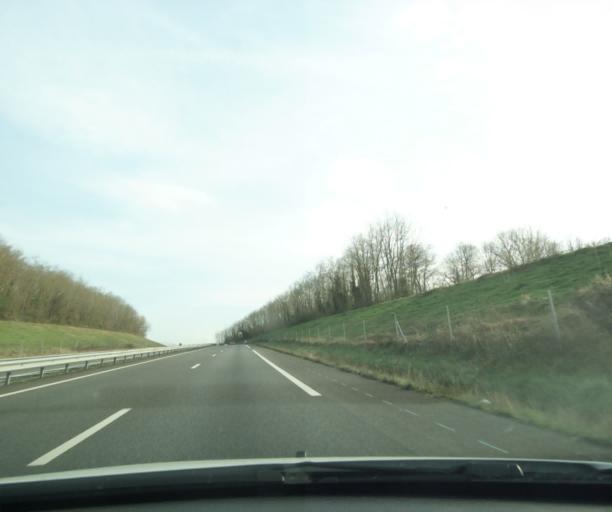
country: FR
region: Midi-Pyrenees
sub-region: Departement des Hautes-Pyrenees
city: Barbazan-Debat
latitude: 43.2039
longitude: 0.1467
